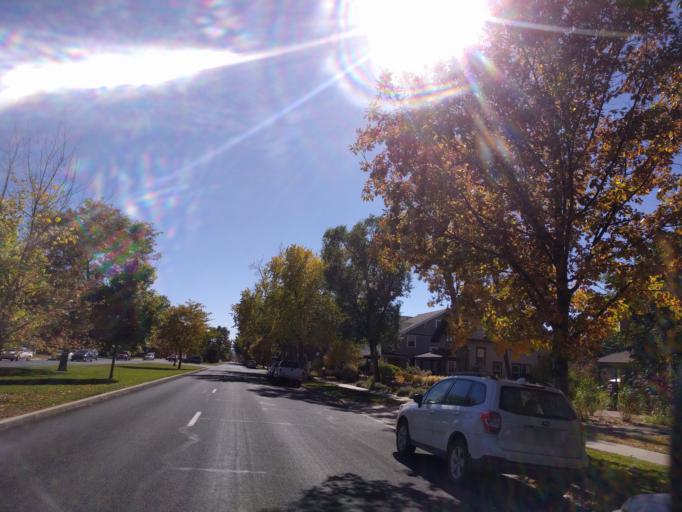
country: US
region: Colorado
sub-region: El Paso County
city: Colorado Springs
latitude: 38.8448
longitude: -104.8249
